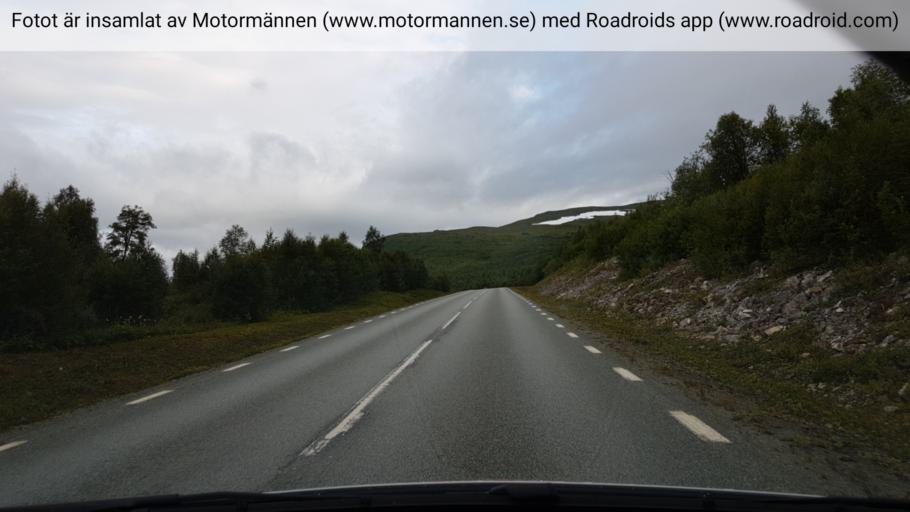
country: NO
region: Nordland
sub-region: Rana
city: Mo i Rana
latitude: 66.1230
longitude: 14.7838
